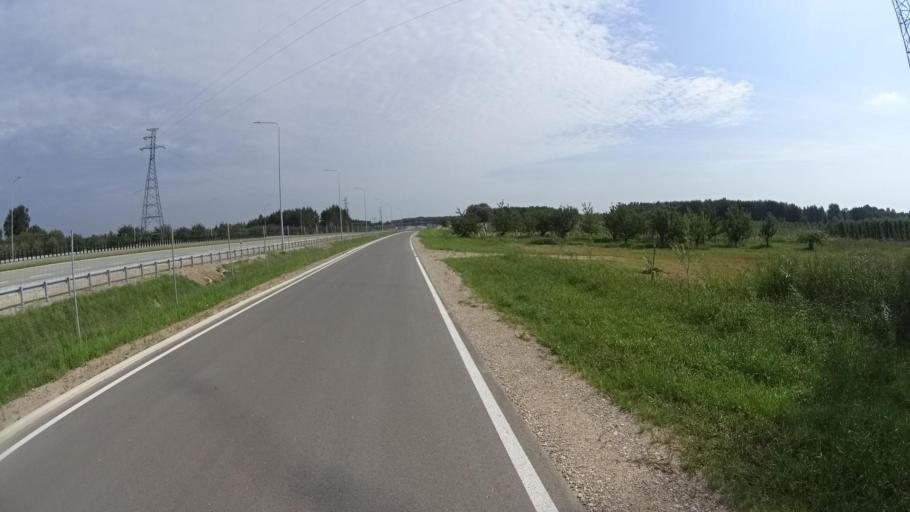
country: PL
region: Masovian Voivodeship
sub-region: Powiat piaseczynski
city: Tarczyn
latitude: 51.9528
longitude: 20.8475
